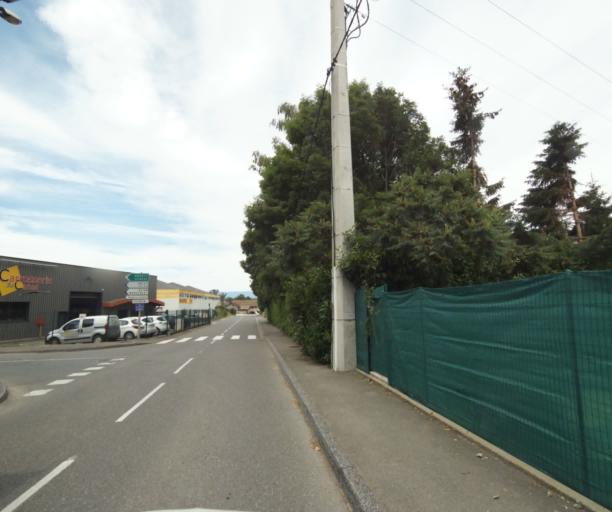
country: FR
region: Rhone-Alpes
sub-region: Departement de la Haute-Savoie
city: Anthy-sur-Leman
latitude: 46.3531
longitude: 6.4463
